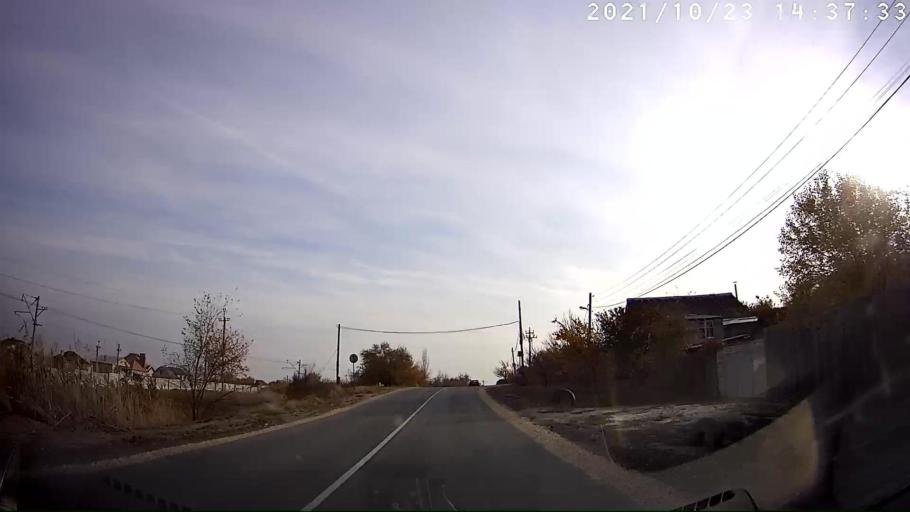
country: RU
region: Volgograd
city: Krasnoslobodsk
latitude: 48.4972
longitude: 44.5493
